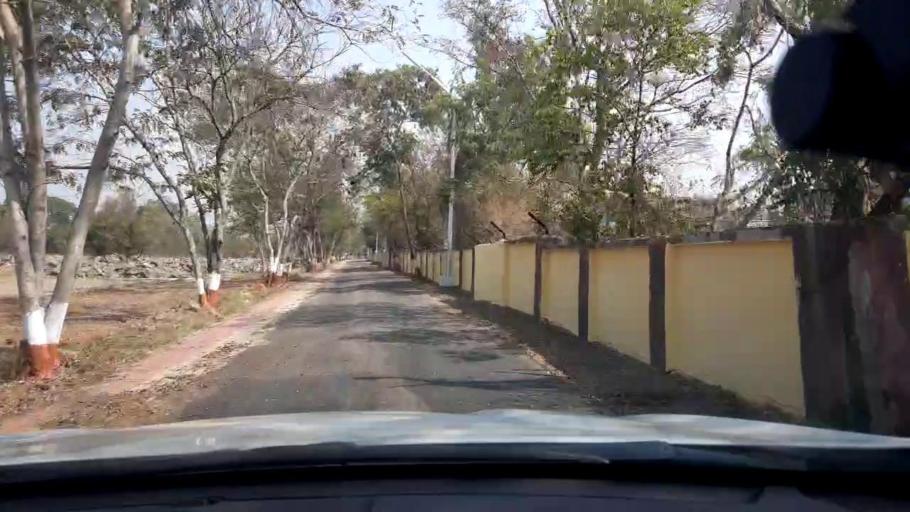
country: IN
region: Maharashtra
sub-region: Pune Division
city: Shivaji Nagar
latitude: 18.5412
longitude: 73.8616
